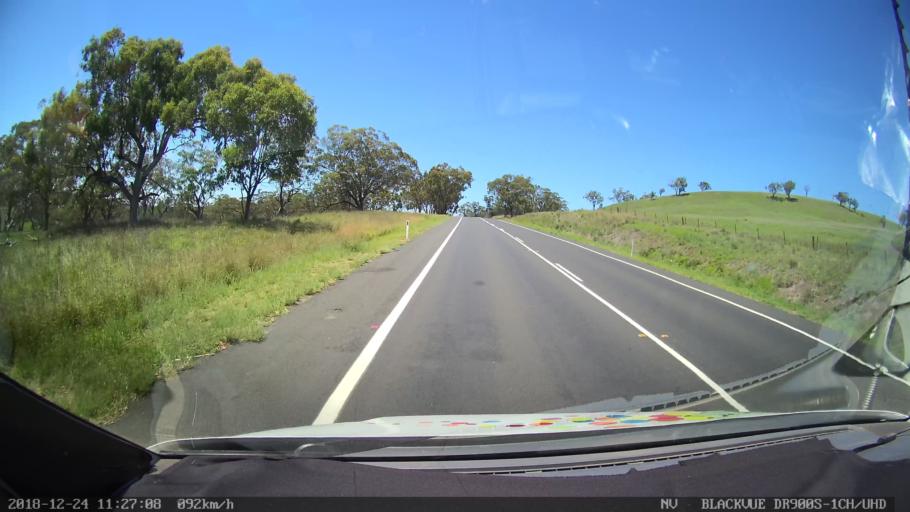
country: AU
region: New South Wales
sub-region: Upper Hunter Shire
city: Merriwa
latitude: -32.1782
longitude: 150.4341
